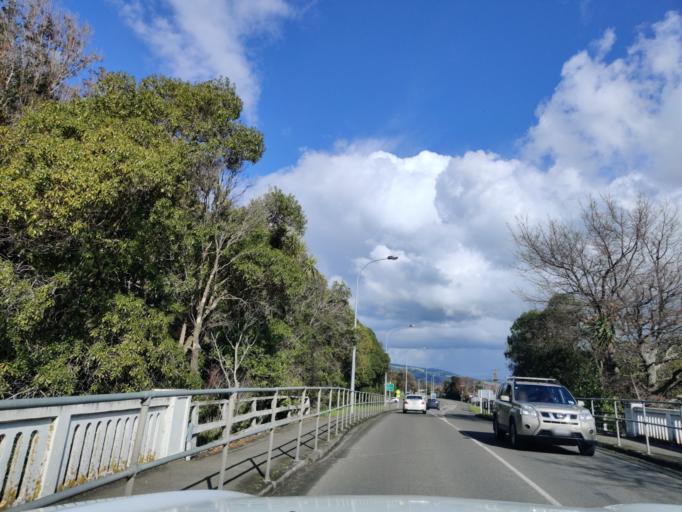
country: NZ
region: Manawatu-Wanganui
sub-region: Palmerston North City
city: Palmerston North
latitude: -40.2961
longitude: 175.7531
